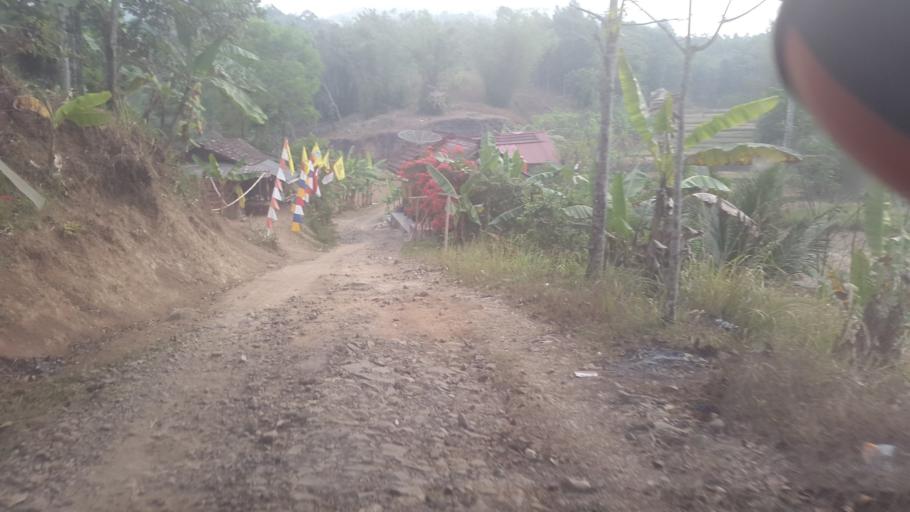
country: ID
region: West Java
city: Sukamaju
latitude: -7.0040
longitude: 106.8860
